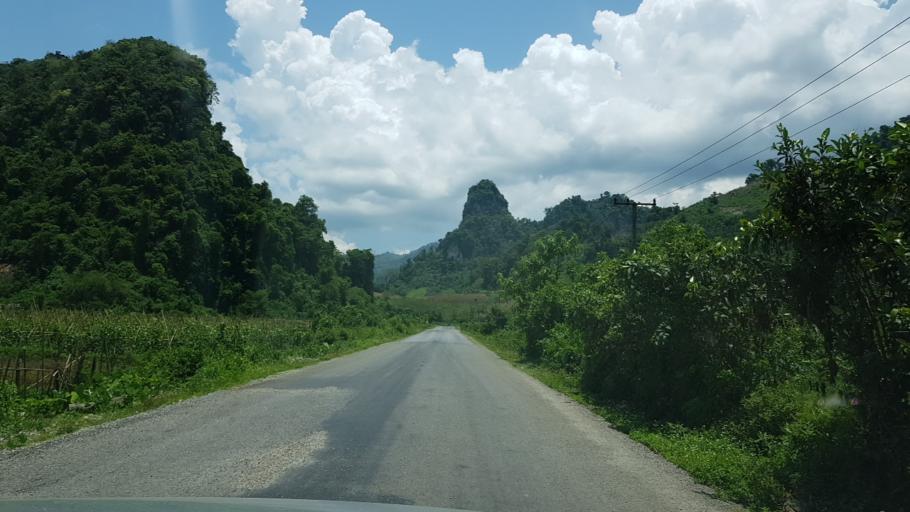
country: LA
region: Vientiane
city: Muang Kasi
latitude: 19.1237
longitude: 102.2549
